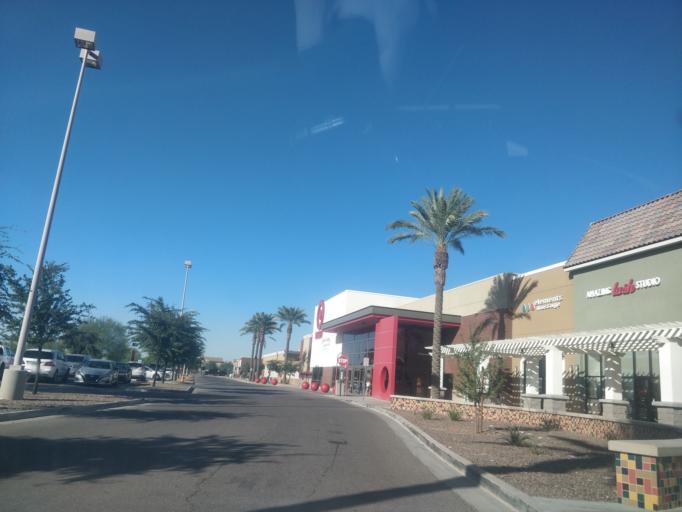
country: US
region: Arizona
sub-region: Maricopa County
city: Sun Lakes
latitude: 33.2495
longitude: -111.8385
